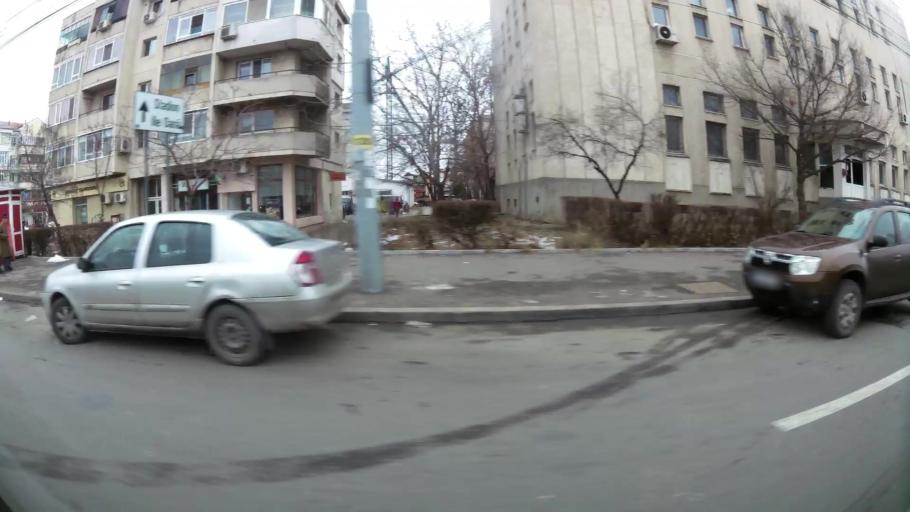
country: RO
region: Prahova
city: Ploiesti
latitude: 44.9338
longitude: 26.0317
